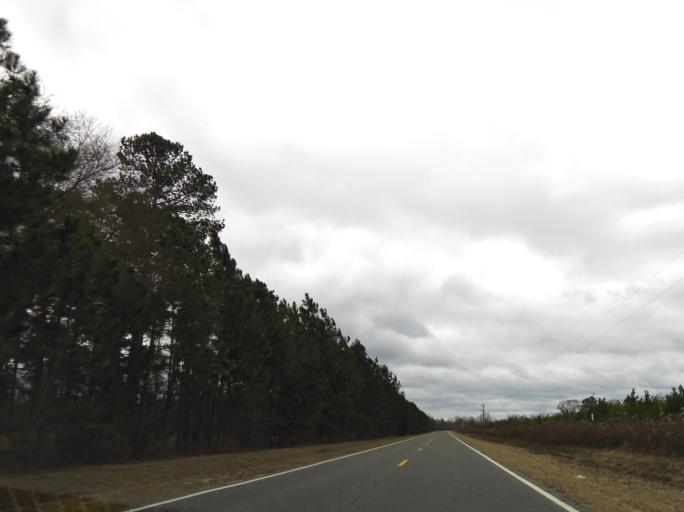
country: US
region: Georgia
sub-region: Bleckley County
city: Cochran
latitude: 32.4689
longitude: -83.3791
